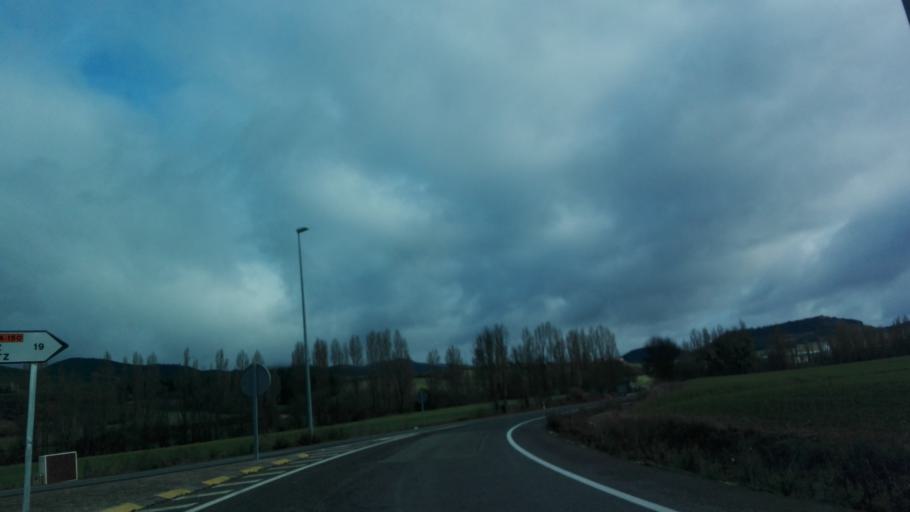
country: ES
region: Navarre
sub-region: Provincia de Navarra
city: Egues-Uharte
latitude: 42.8284
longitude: -1.5737
